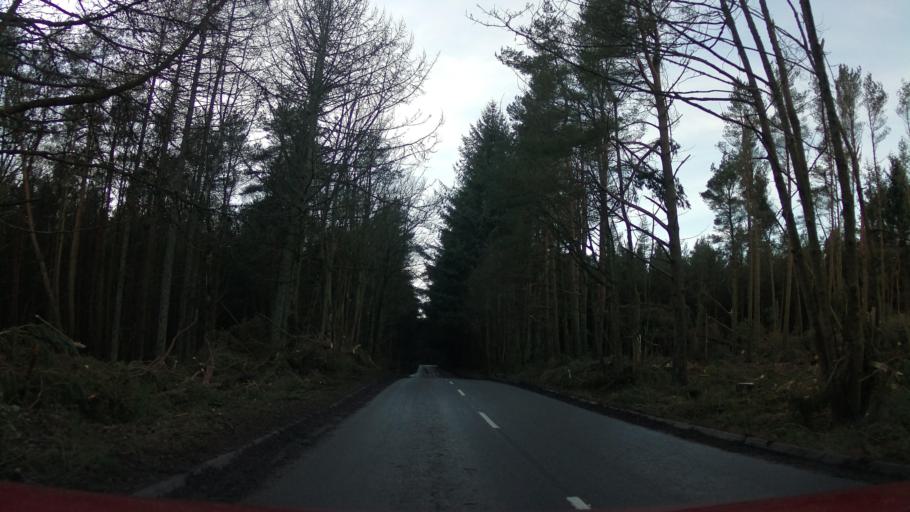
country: GB
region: Scotland
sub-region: Angus
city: Letham
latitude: 56.5848
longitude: -2.8264
